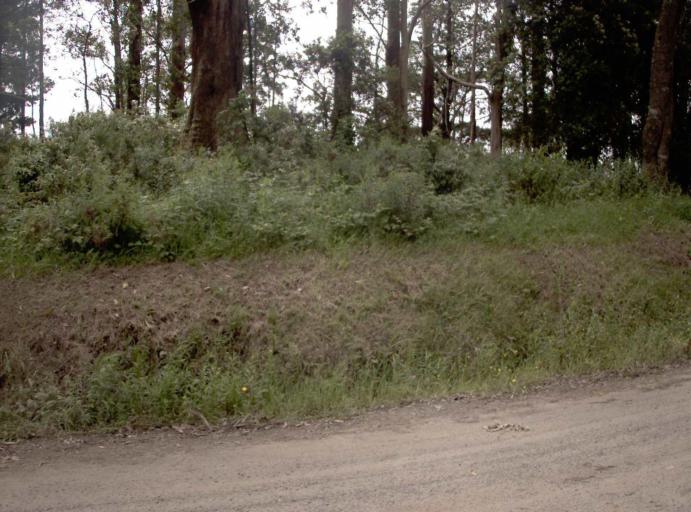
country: AU
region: Victoria
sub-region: Latrobe
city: Traralgon
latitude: -38.3800
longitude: 146.6677
